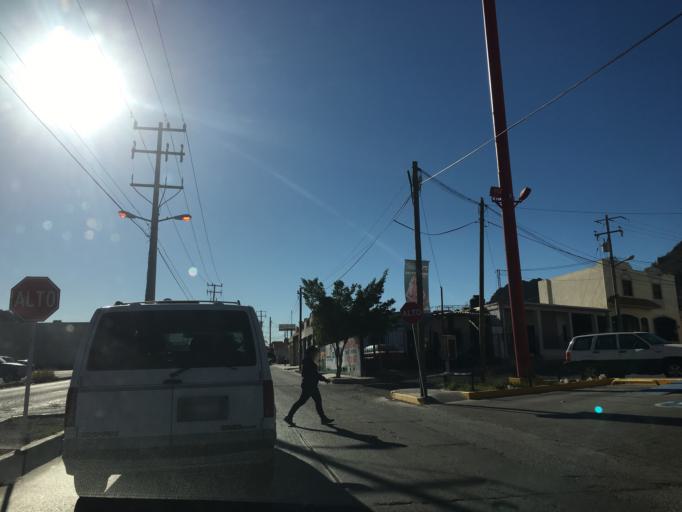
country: MX
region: Sonora
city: Heroica Guaymas
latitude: 27.9207
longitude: -110.9162
